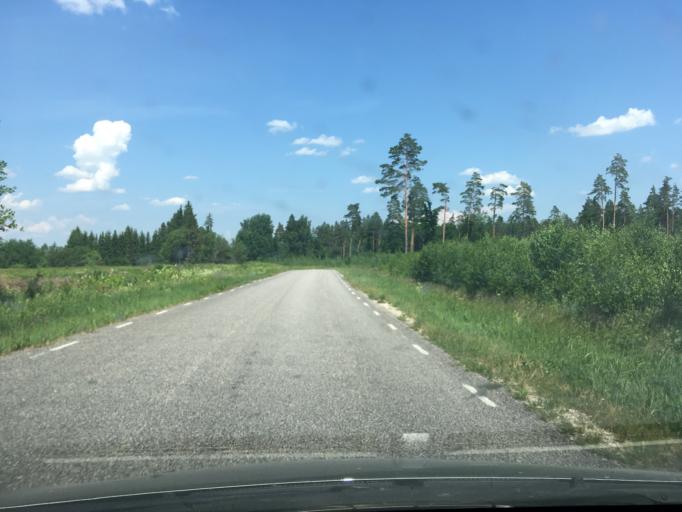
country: EE
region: Raplamaa
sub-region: Maerjamaa vald
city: Marjamaa
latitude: 58.7525
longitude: 24.4101
